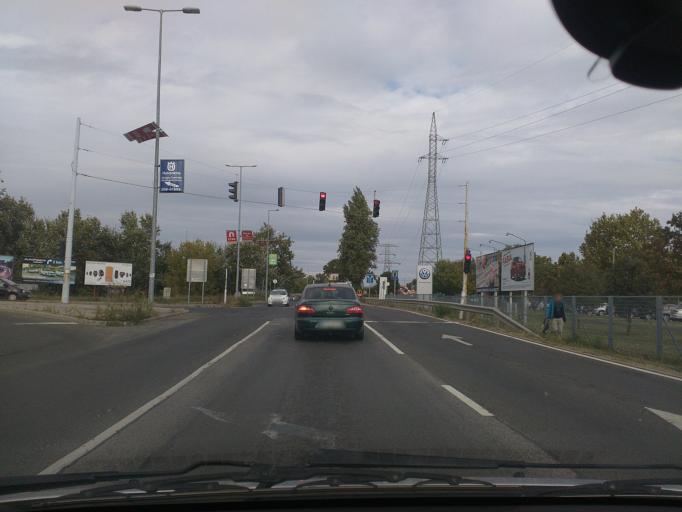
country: HU
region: Budapest
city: Budapest XVIII. keruelet
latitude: 47.4239
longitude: 19.1566
